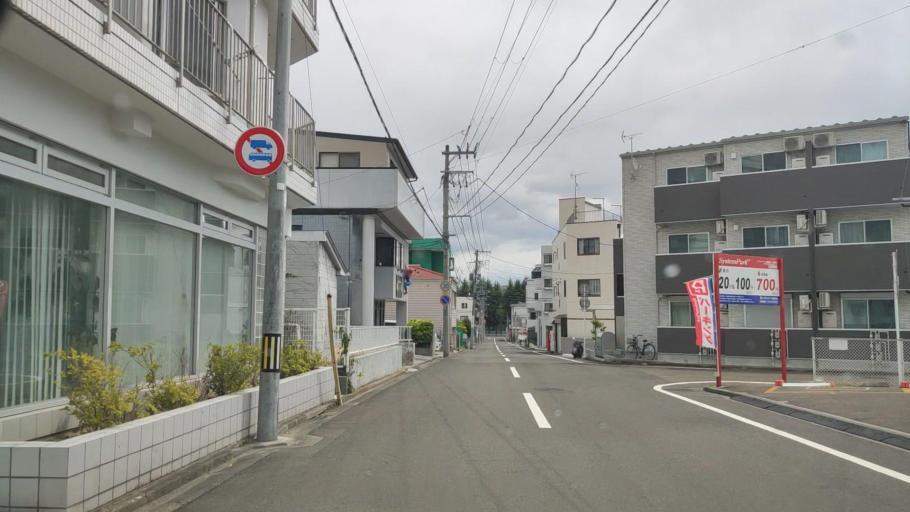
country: JP
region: Miyagi
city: Sendai-shi
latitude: 38.2578
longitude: 140.8985
